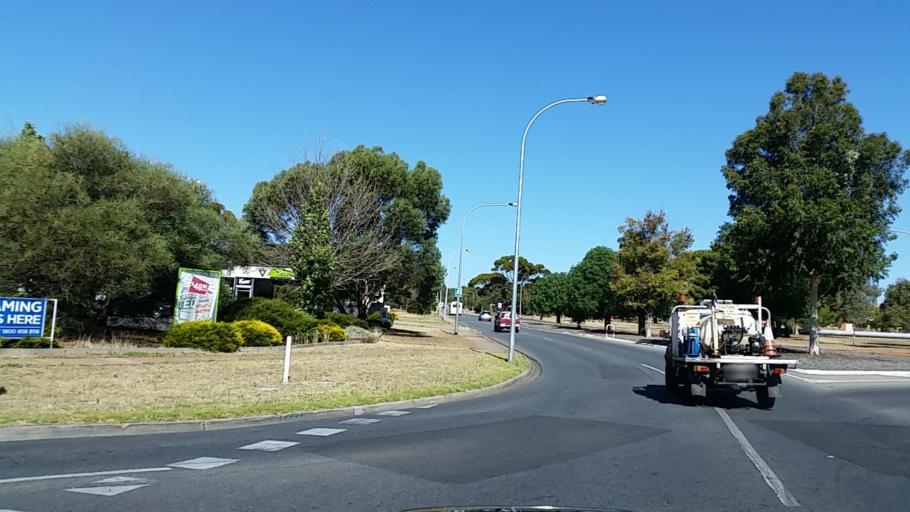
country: AU
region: South Australia
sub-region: Salisbury
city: Elizabeth
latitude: -34.7069
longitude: 138.6914
